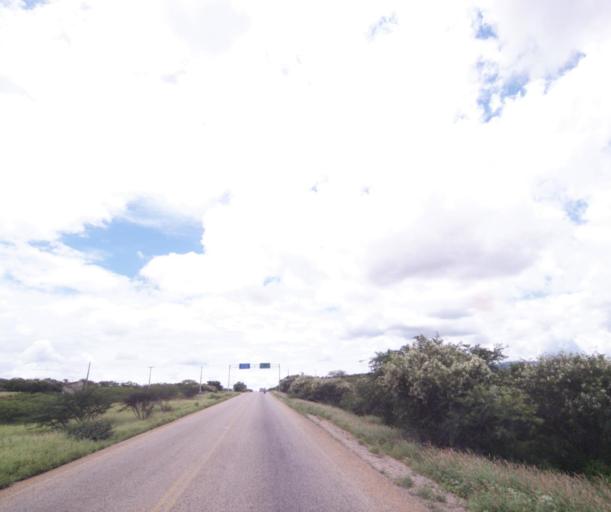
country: BR
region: Bahia
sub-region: Brumado
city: Brumado
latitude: -14.2135
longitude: -41.6406
